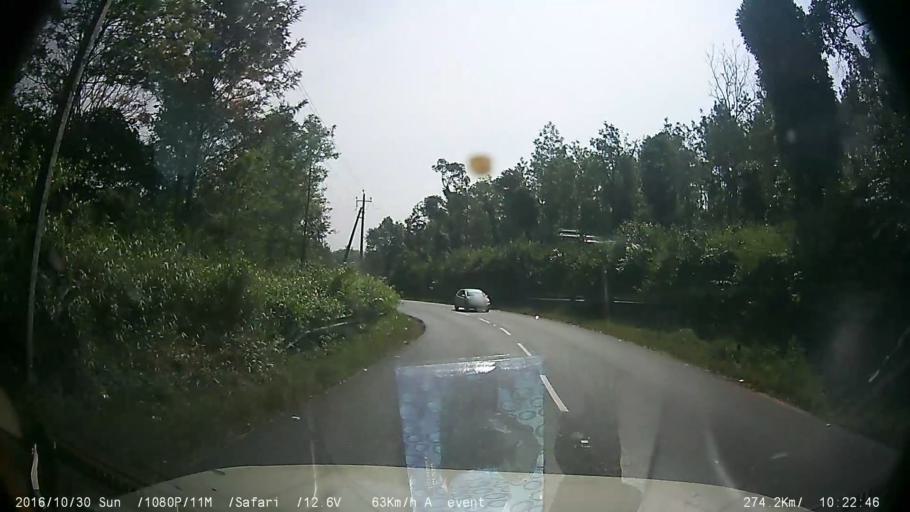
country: IN
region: Karnataka
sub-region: Kodagu
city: Madikeri
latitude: 12.4302
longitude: 75.7674
